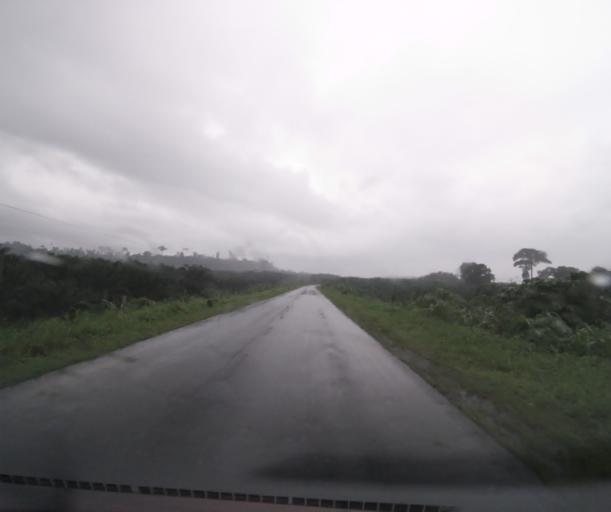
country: CM
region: South-West Province
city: Idenao
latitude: 4.1701
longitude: 8.9965
